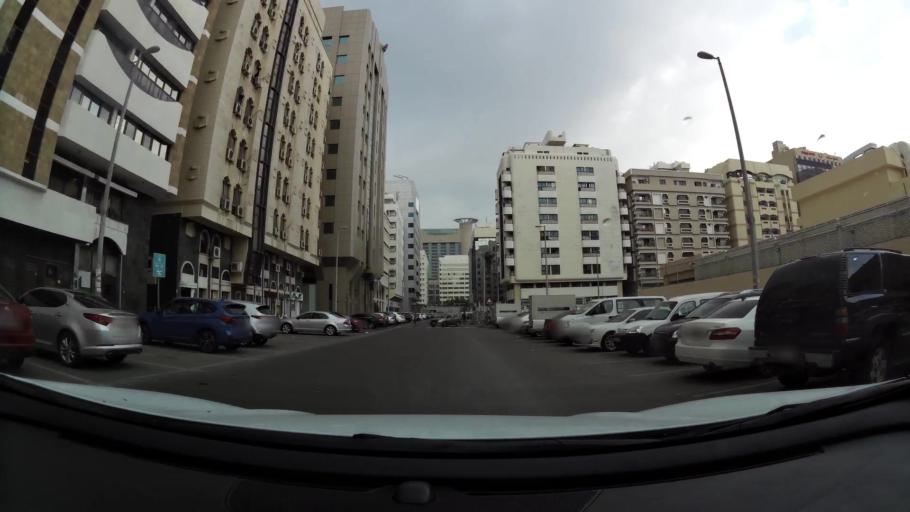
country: AE
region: Abu Dhabi
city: Abu Dhabi
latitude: 24.4926
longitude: 54.3802
